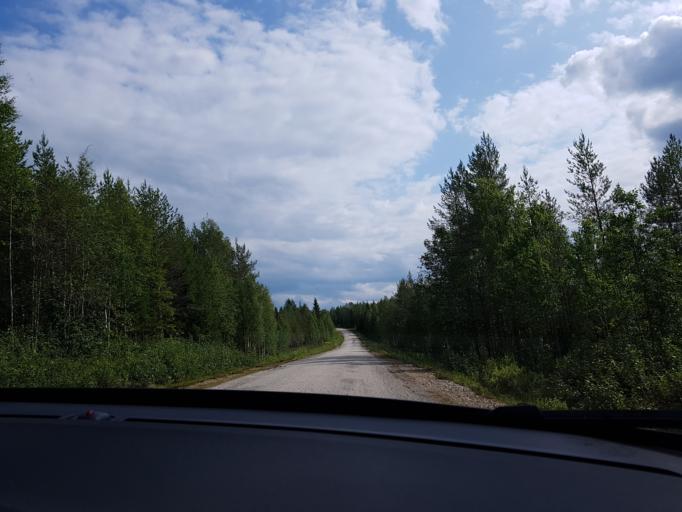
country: FI
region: Kainuu
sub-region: Kehys-Kainuu
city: Kuhmo
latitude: 64.4391
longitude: 29.7062
